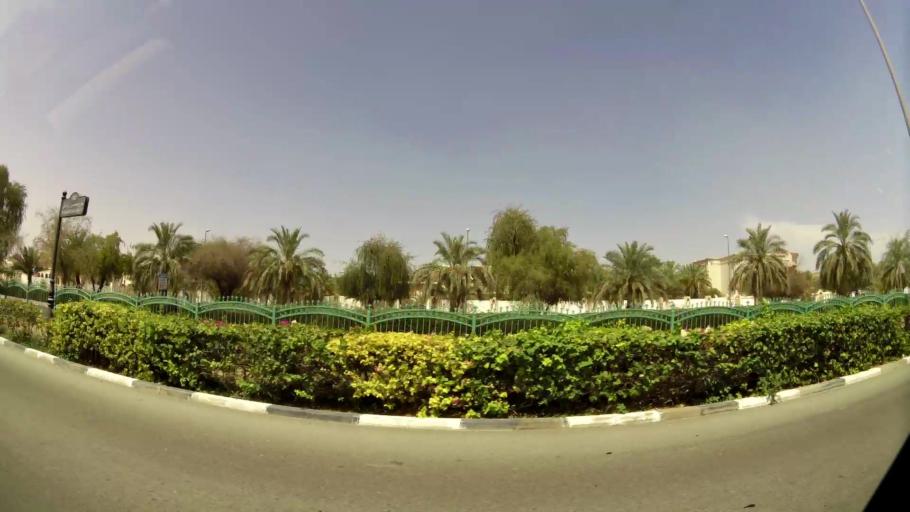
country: AE
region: Abu Dhabi
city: Al Ain
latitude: 24.2373
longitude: 55.7044
